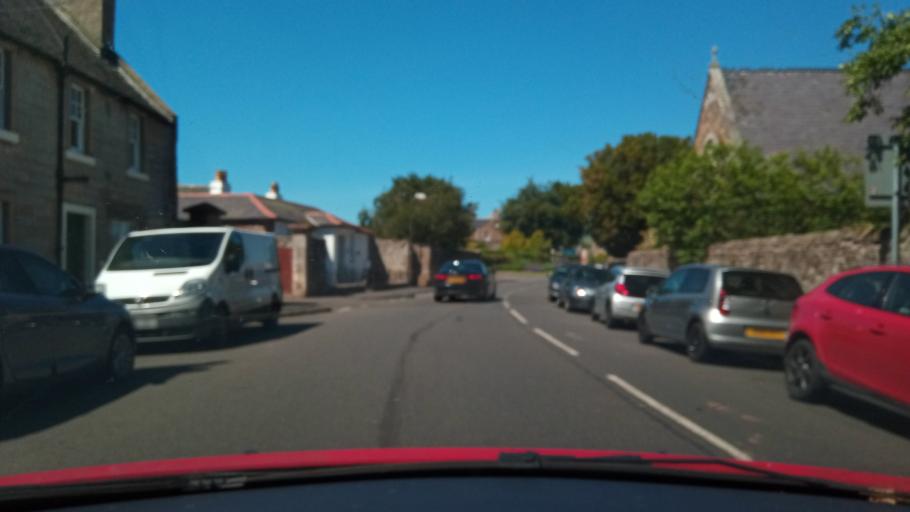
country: GB
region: Scotland
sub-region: East Lothian
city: Haddington
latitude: 55.9521
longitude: -2.7740
